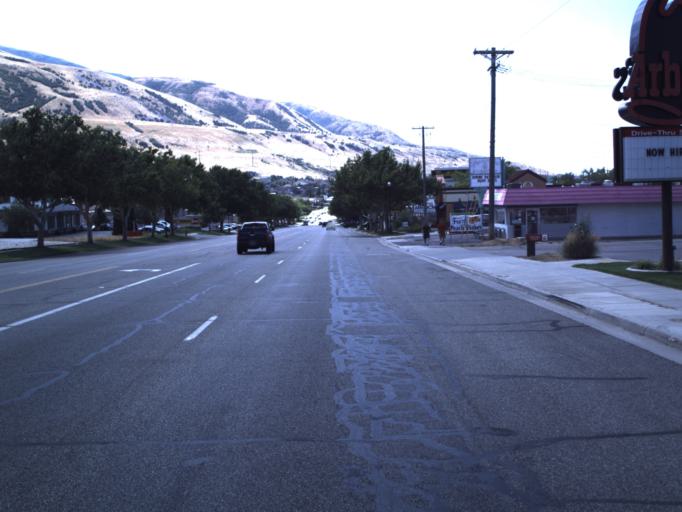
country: US
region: Utah
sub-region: Box Elder County
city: Brigham City
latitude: 41.4946
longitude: -112.0162
